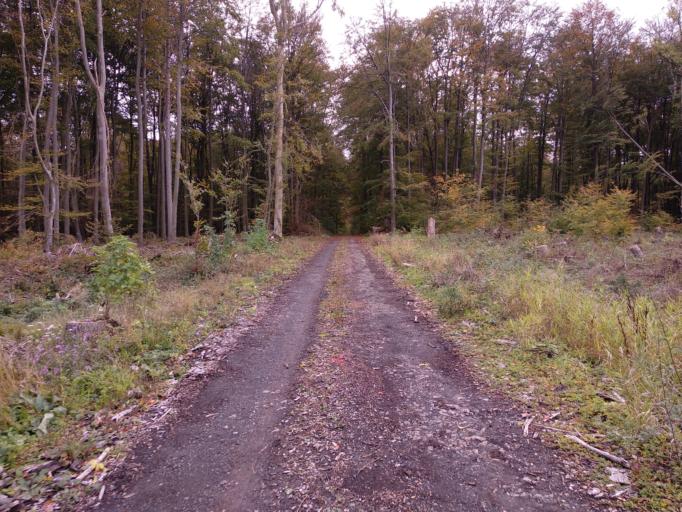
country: DE
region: North Rhine-Westphalia
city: Beverungen
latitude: 51.6669
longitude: 9.3295
